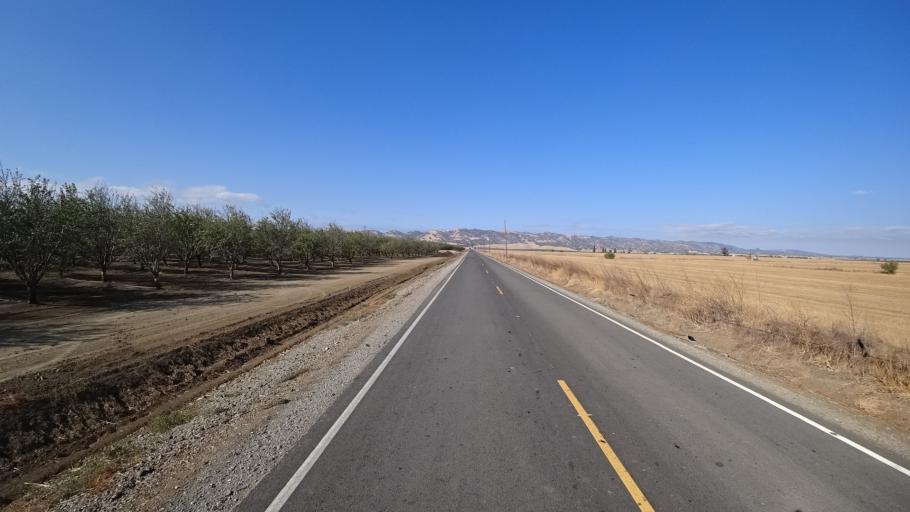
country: US
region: California
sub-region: Yolo County
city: Esparto
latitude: 38.7811
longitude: -122.0324
